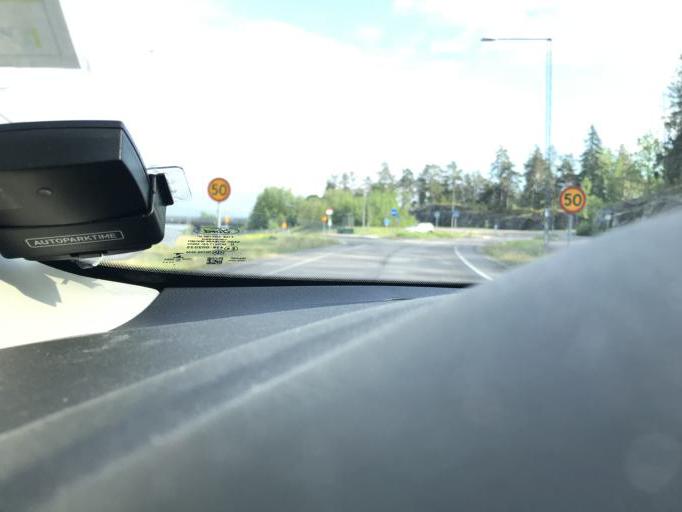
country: SE
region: Stockholm
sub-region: Botkyrka Kommun
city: Tumba
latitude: 59.2110
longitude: 17.8323
